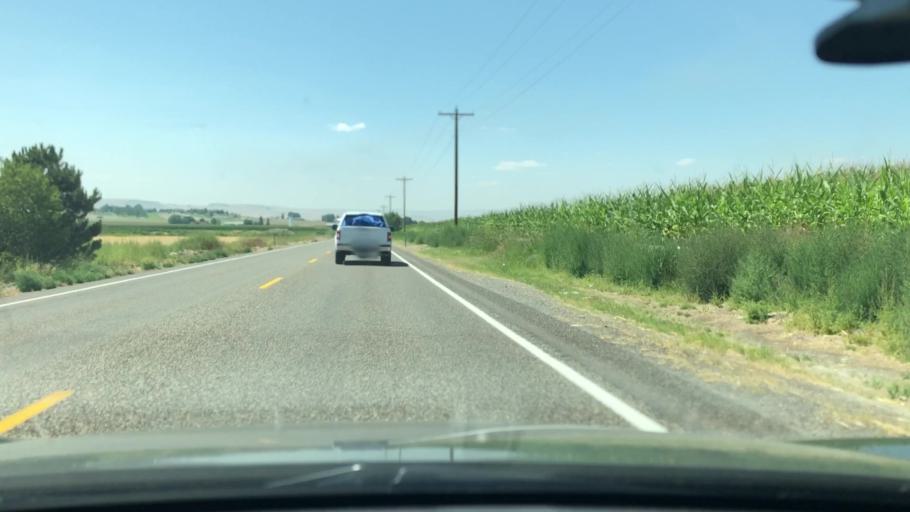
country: US
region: Idaho
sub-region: Owyhee County
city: Marsing
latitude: 43.5453
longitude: -116.8751
